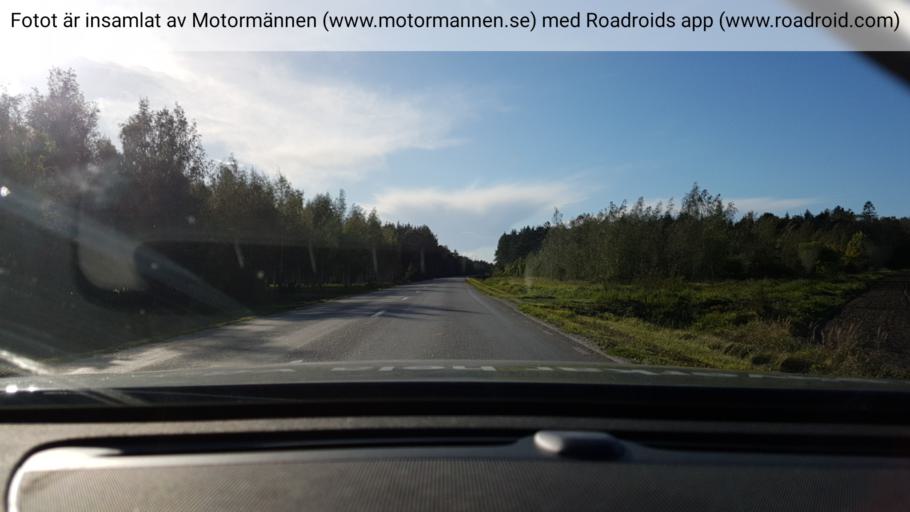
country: SE
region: Gotland
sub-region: Gotland
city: Klintehamn
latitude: 57.3799
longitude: 18.2172
